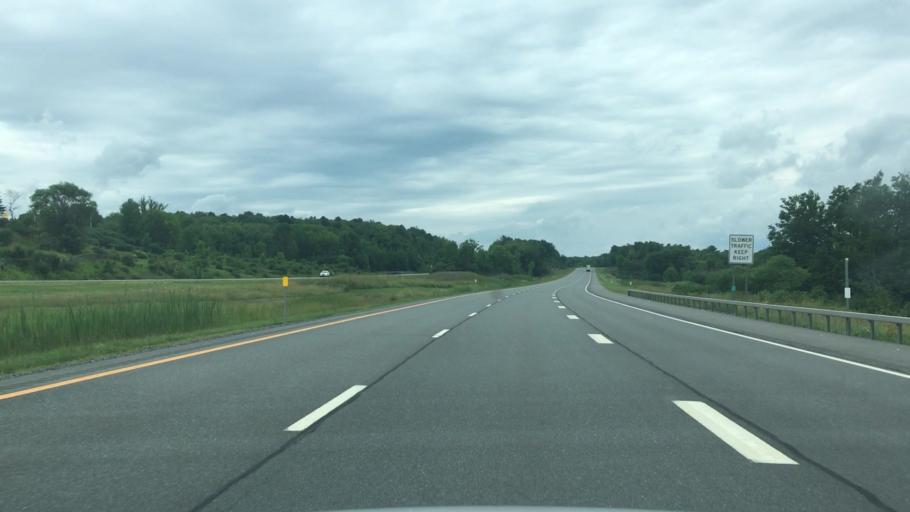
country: US
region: New York
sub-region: Schoharie County
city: Schoharie
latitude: 42.7280
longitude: -74.1980
